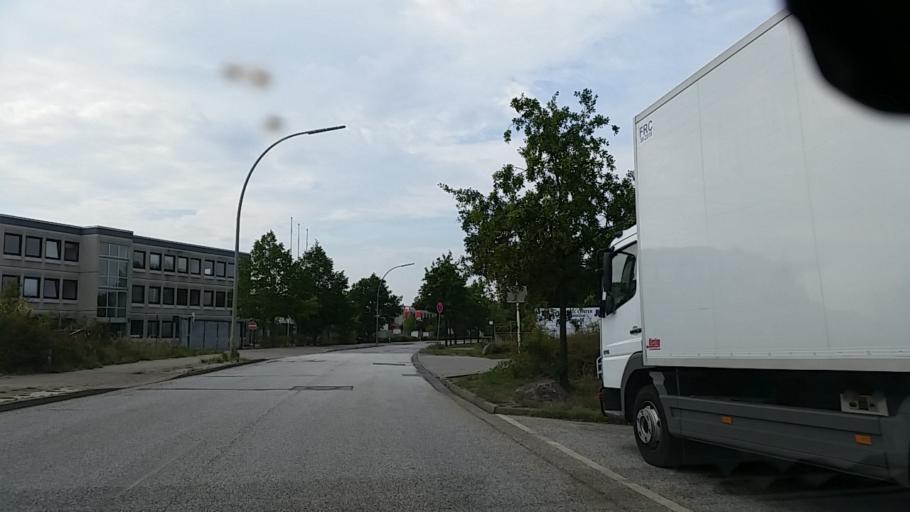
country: DE
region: Hamburg
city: Wandsbek
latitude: 53.4949
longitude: 10.1171
